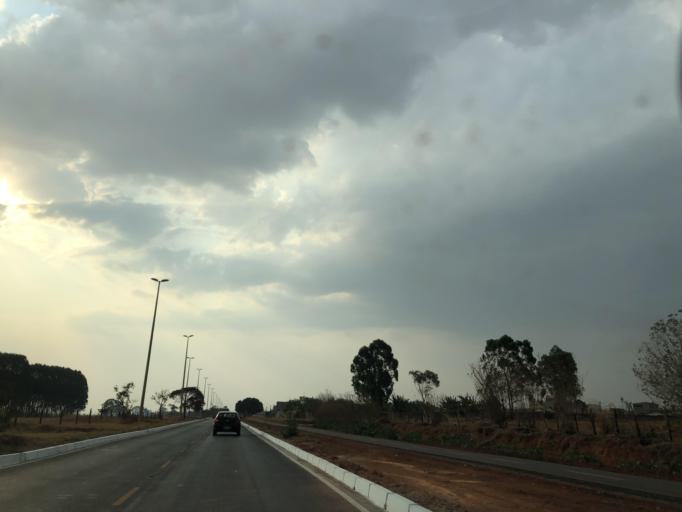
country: BR
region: Federal District
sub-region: Brasilia
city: Brasilia
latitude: -15.9285
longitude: -48.0500
